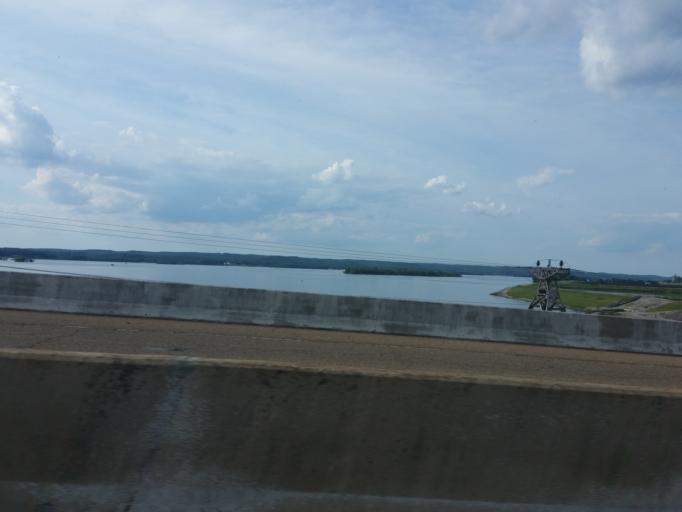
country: US
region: Tennessee
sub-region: Humphreys County
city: New Johnsonville
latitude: 36.0176
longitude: -87.9986
